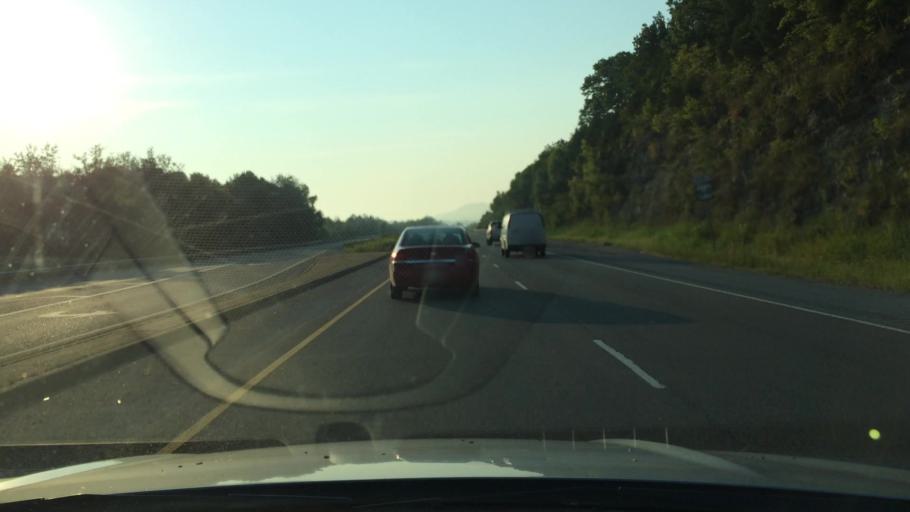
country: US
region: Tennessee
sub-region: Giles County
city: Pulaski
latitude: 35.1701
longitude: -87.0509
